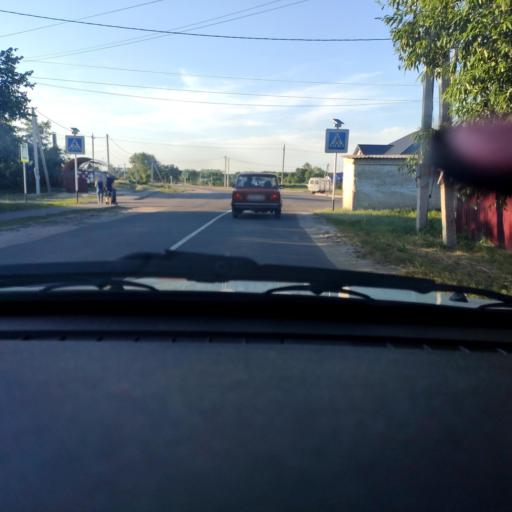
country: RU
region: Voronezj
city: Ramon'
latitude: 51.9027
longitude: 39.2859
